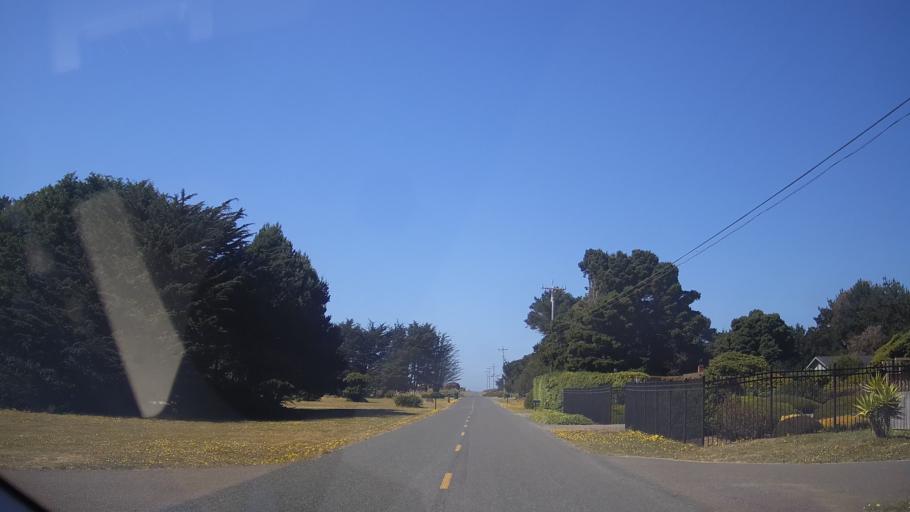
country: US
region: California
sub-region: Mendocino County
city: Fort Bragg
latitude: 39.4203
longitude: -123.8138
